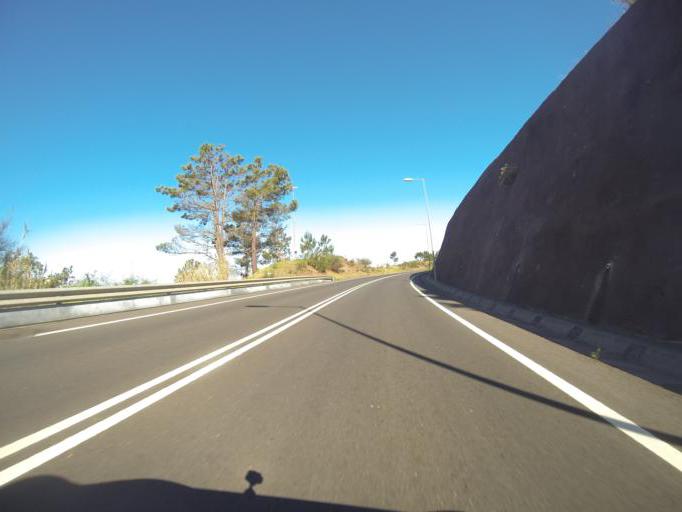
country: PT
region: Madeira
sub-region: Calheta
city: Estreito da Calheta
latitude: 32.7527
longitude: -17.2128
